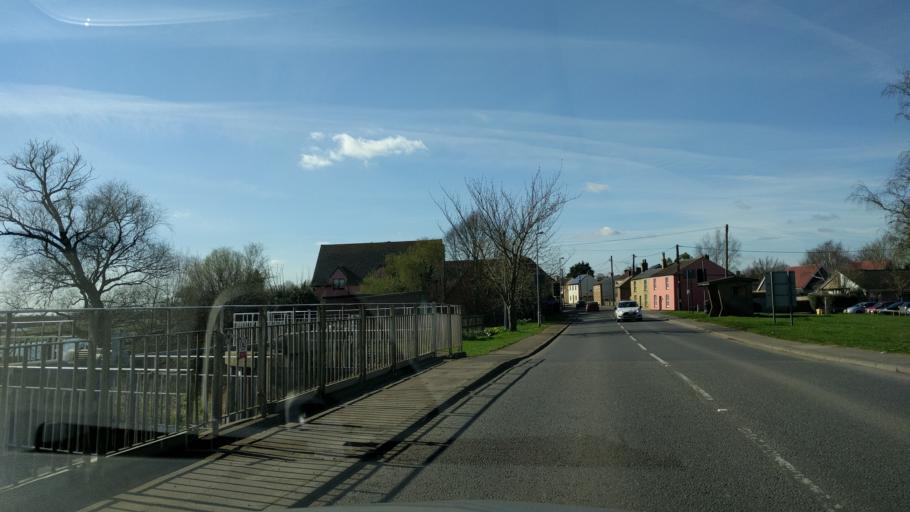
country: GB
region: England
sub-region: Cambridgeshire
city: Earith
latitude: 52.3539
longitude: 0.0379
